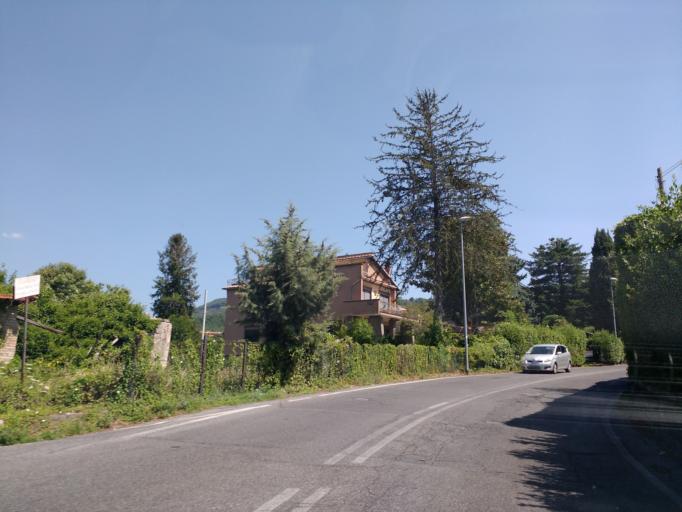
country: IT
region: Latium
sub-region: Citta metropolitana di Roma Capitale
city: Rocca di Papa
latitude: 41.7737
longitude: 12.6992
